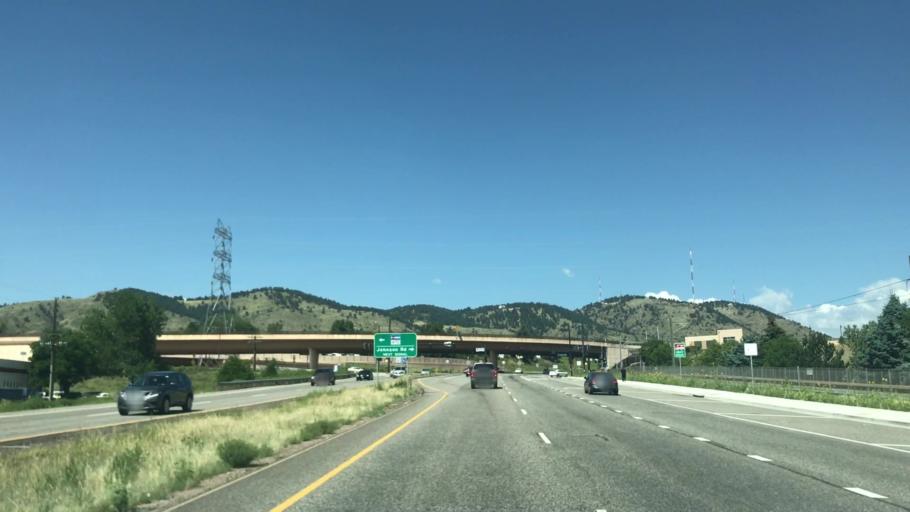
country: US
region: Colorado
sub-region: Jefferson County
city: West Pleasant View
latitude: 39.7252
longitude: -105.1962
